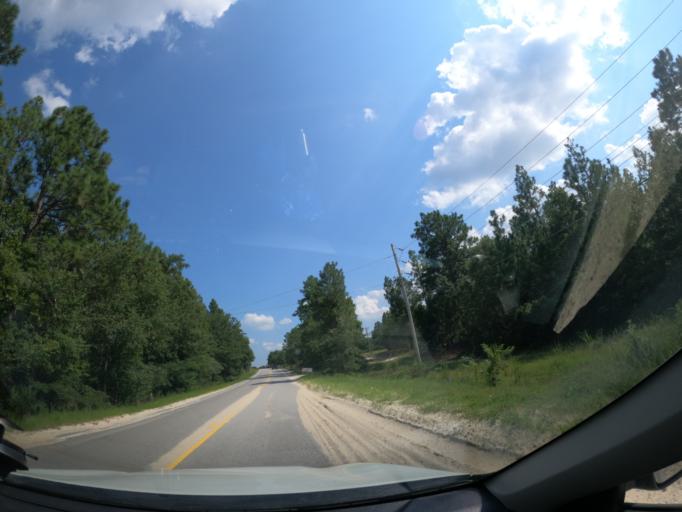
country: US
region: South Carolina
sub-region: Lexington County
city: South Congaree
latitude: 33.8978
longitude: -81.1572
